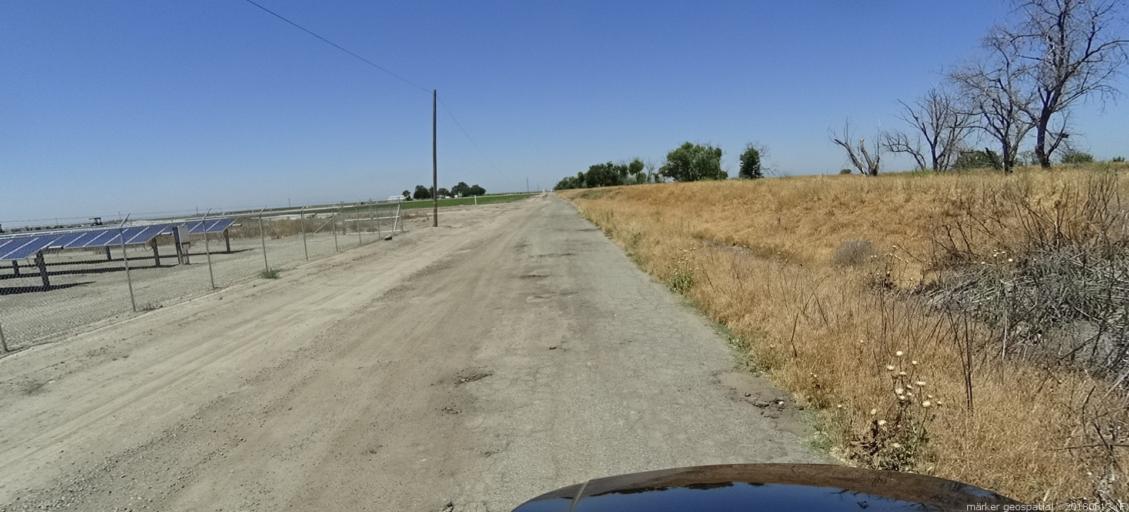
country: US
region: California
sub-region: Madera County
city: Chowchilla
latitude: 36.9955
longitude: -120.3499
